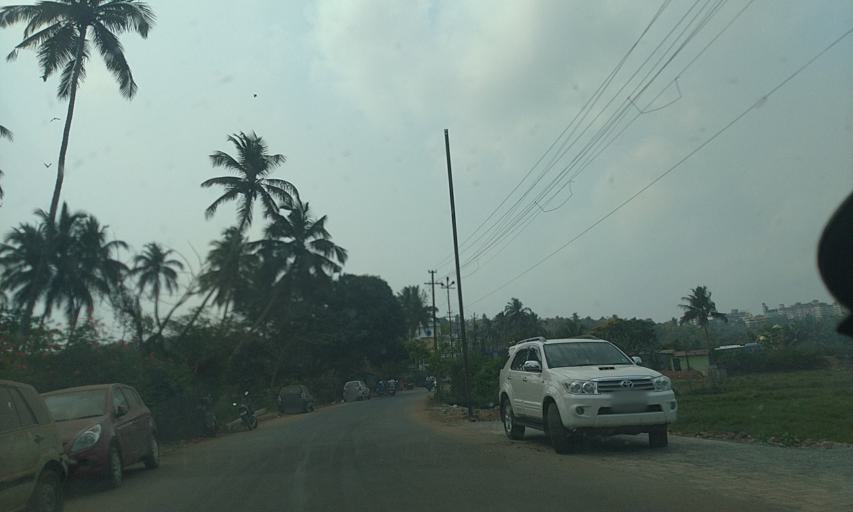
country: IN
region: Goa
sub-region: North Goa
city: Taleigao
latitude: 15.4700
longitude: 73.8279
